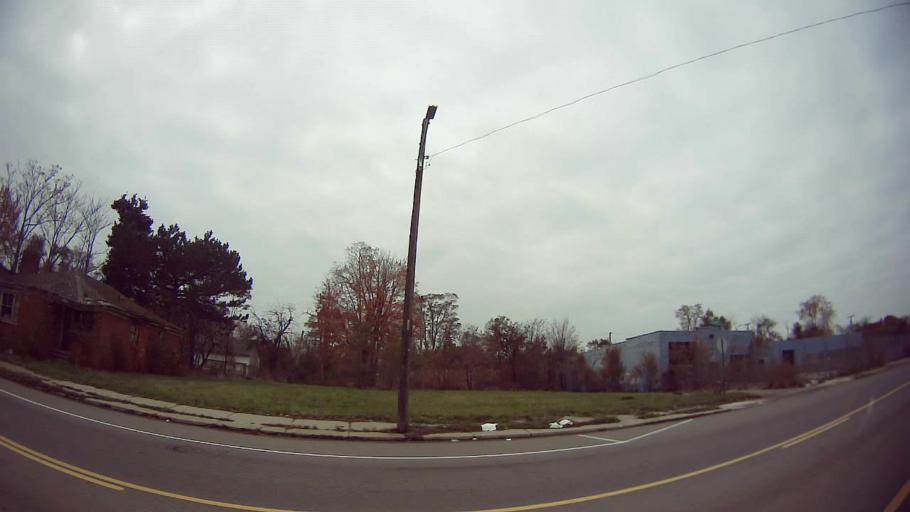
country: US
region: Michigan
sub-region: Wayne County
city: Highland Park
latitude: 42.4242
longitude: -83.0674
